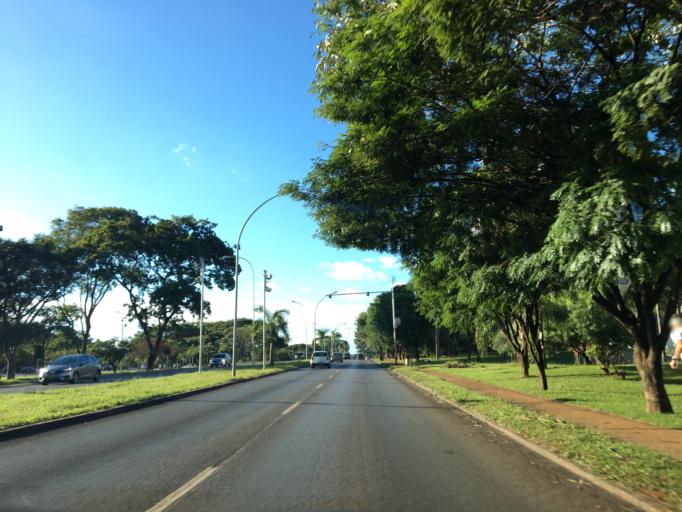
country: BR
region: Federal District
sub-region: Brasilia
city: Brasilia
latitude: -15.7563
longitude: -47.8867
